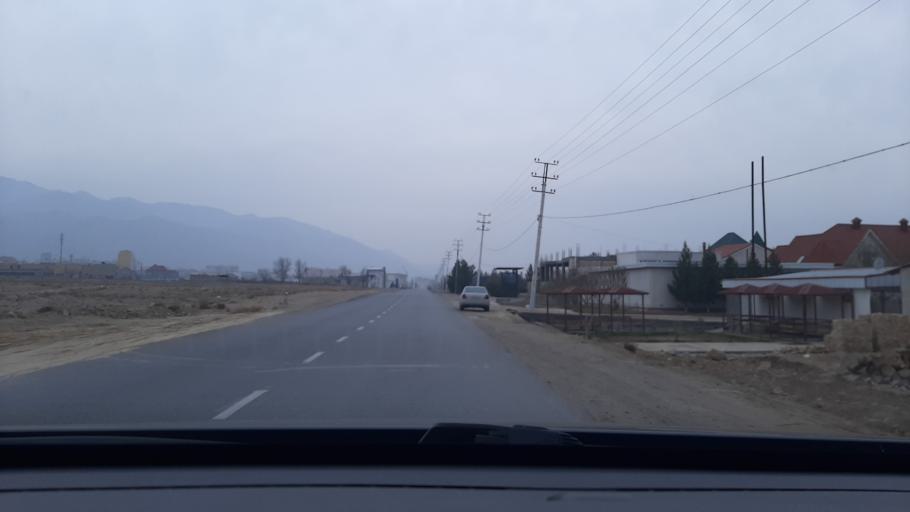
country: TJ
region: Viloyati Sughd
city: Khujand
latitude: 40.2745
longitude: 69.5783
